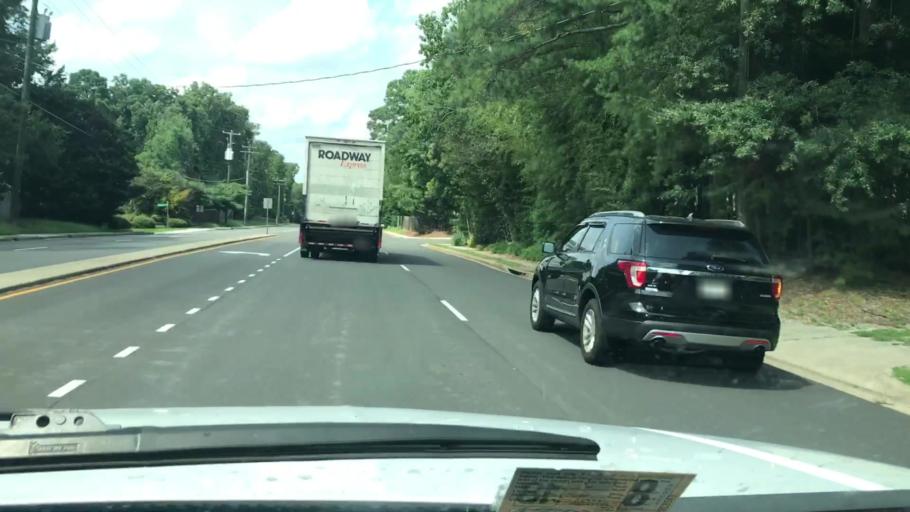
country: US
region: Virginia
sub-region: Henrico County
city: Short Pump
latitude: 37.6093
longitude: -77.6069
